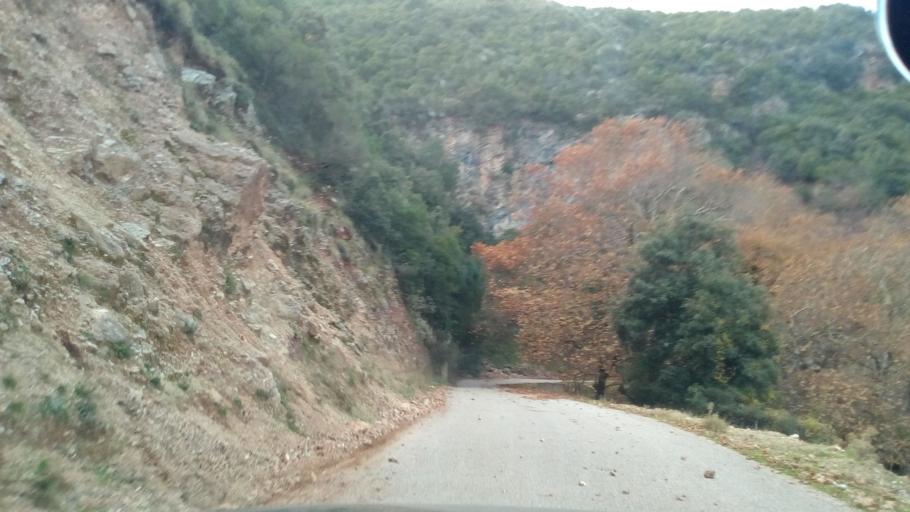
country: GR
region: West Greece
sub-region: Nomos Aitolias kai Akarnanias
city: Nafpaktos
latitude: 38.4312
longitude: 21.8206
